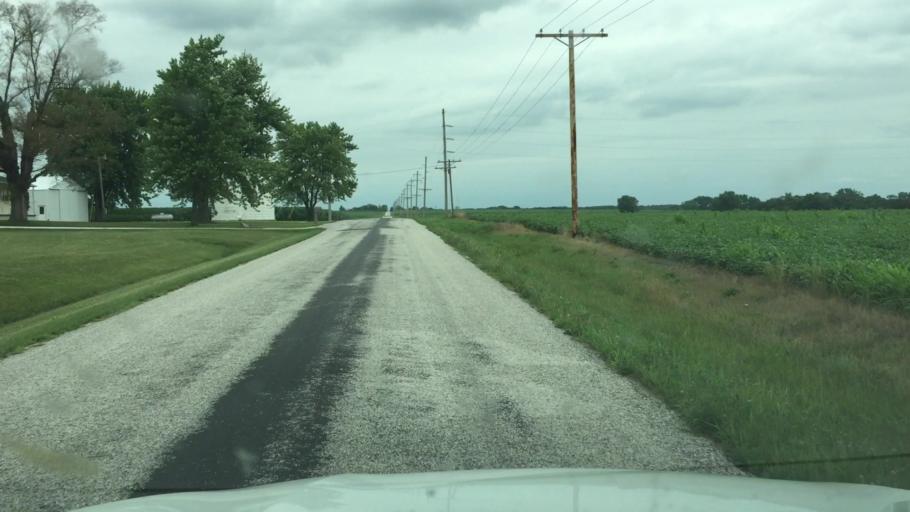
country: US
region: Illinois
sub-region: Hancock County
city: Carthage
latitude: 40.3082
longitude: -91.0829
